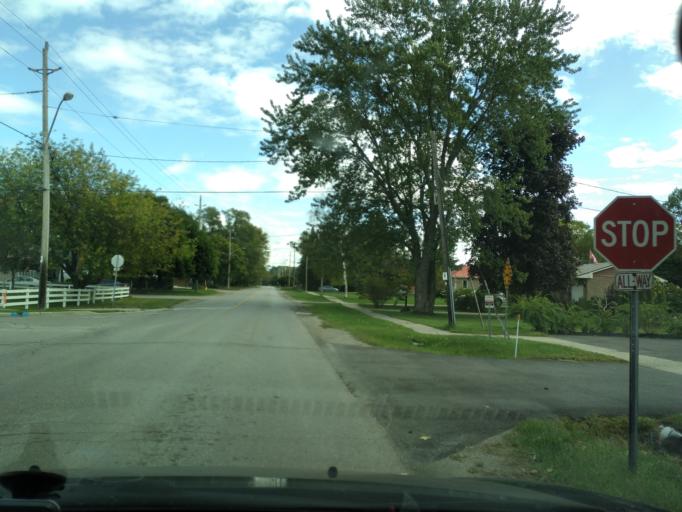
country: CA
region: Ontario
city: Newmarket
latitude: 44.1066
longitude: -79.5077
